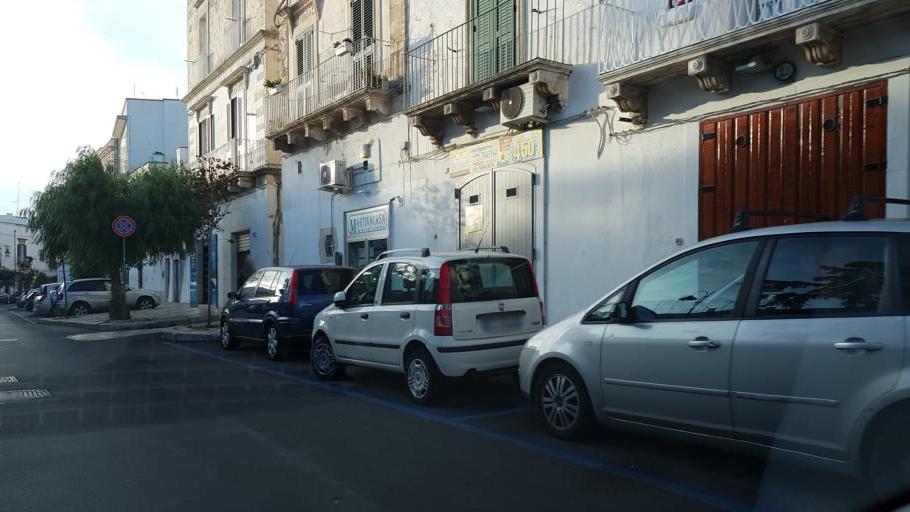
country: IT
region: Apulia
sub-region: Provincia di Taranto
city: Martina Franca
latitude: 40.7033
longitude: 17.3379
